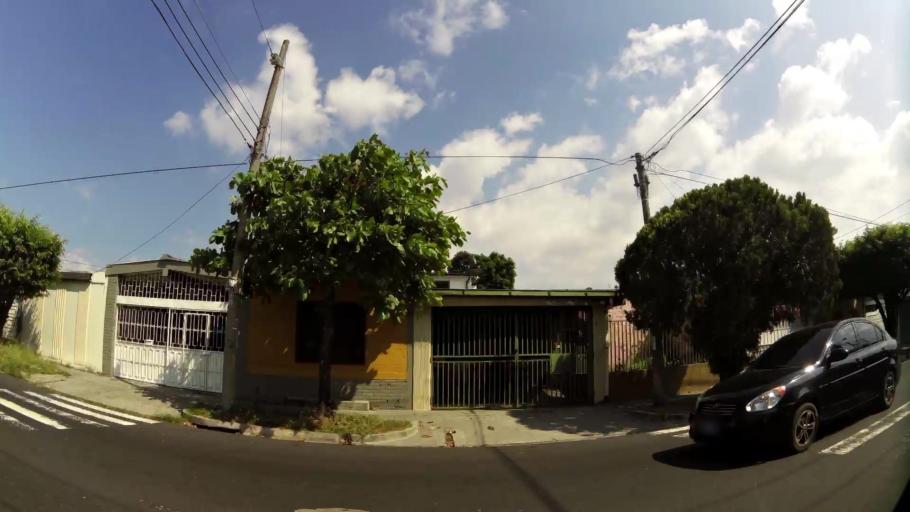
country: SV
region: San Salvador
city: Mejicanos
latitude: 13.7193
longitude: -89.2124
